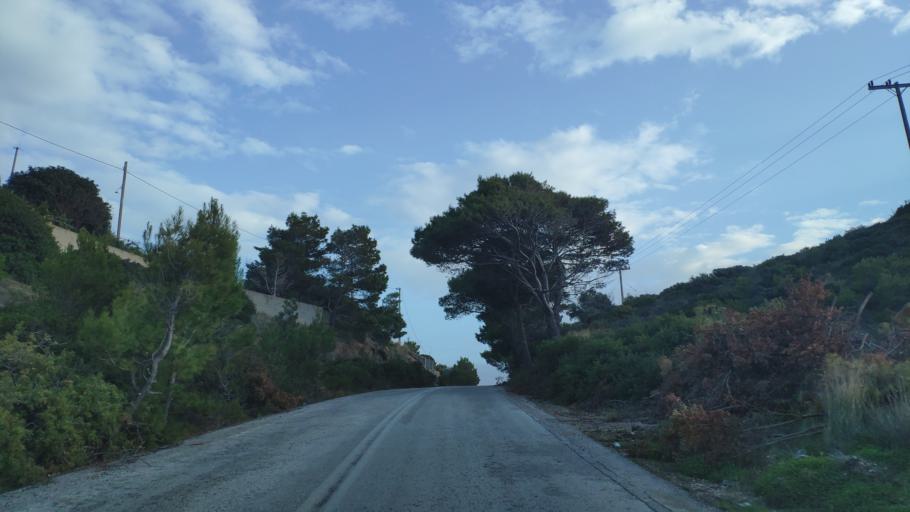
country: GR
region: Attica
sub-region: Nomarchia Anatolikis Attikis
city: Limin Mesoyaias
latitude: 37.9091
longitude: 24.0192
